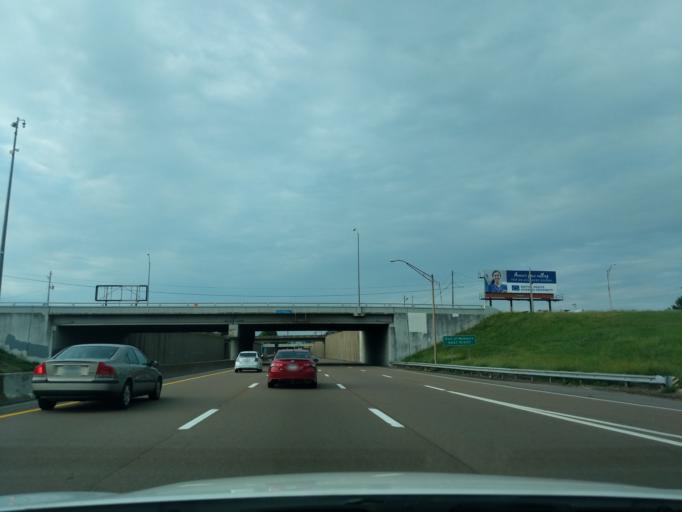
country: US
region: Tennessee
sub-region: Shelby County
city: New South Memphis
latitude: 35.1075
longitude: -90.0756
